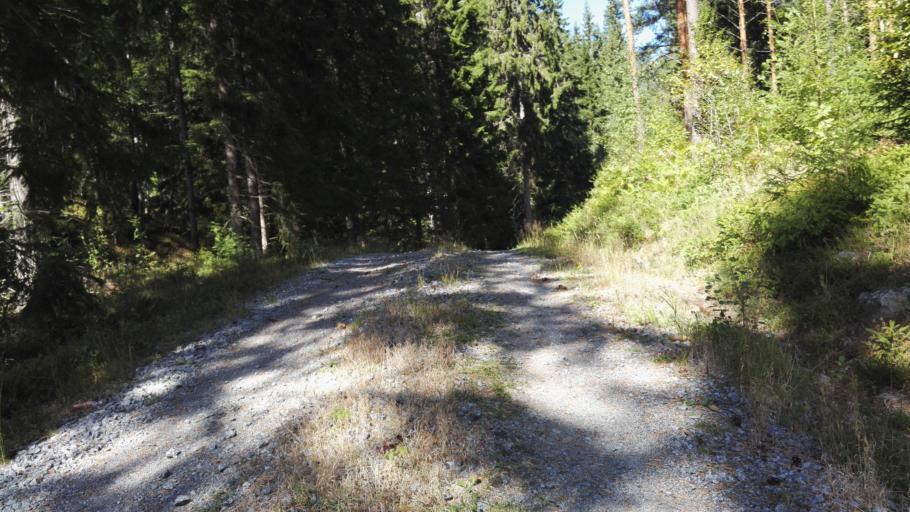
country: SE
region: Joenkoeping
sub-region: Vetlanda Kommun
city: Landsbro
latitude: 57.3240
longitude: 14.8564
